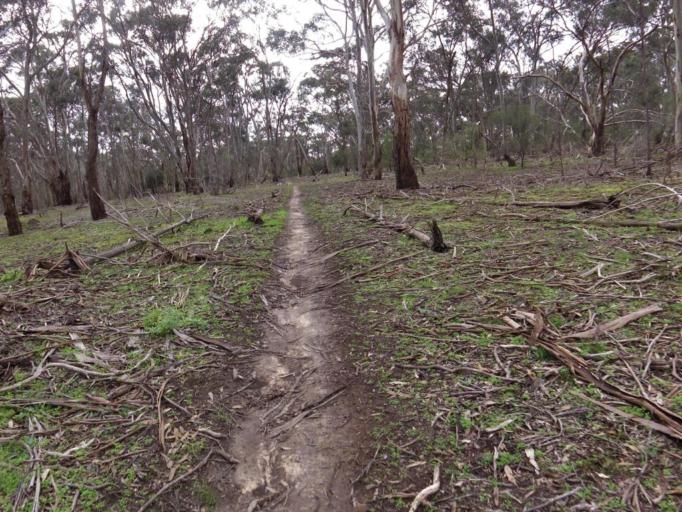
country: AU
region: Victoria
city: Plenty
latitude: -37.6762
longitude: 145.0976
